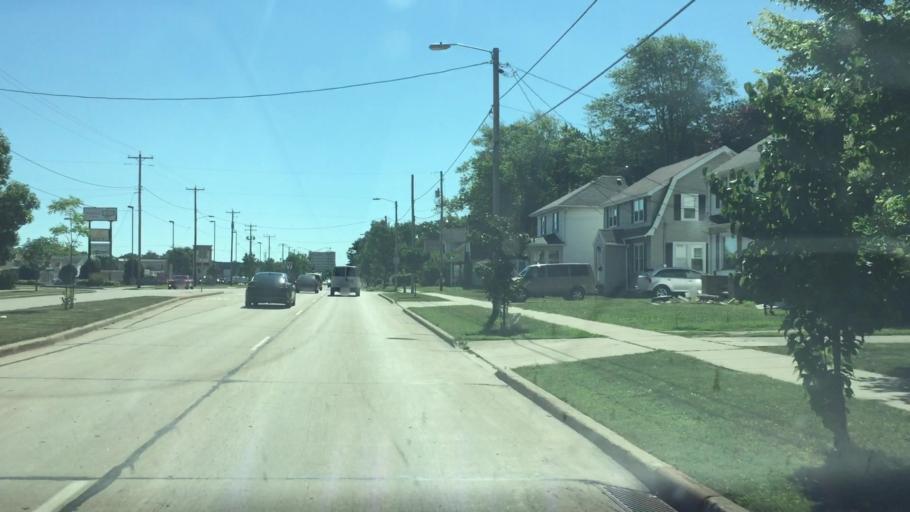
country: US
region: Wisconsin
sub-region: Outagamie County
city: Appleton
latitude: 44.2617
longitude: -88.4292
